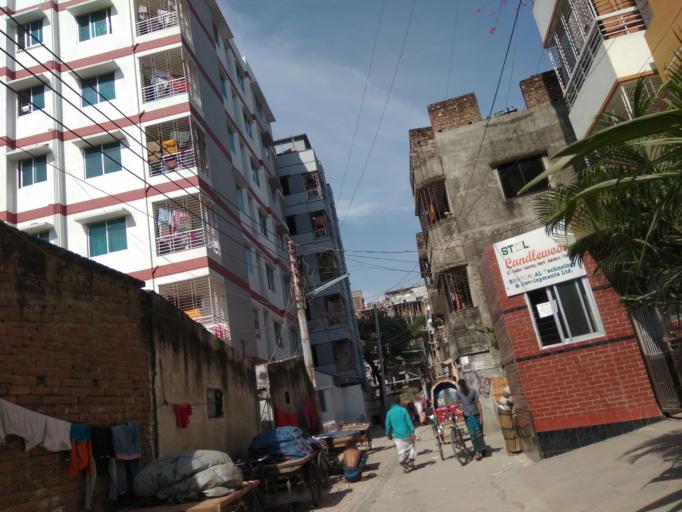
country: BD
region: Dhaka
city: Azimpur
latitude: 23.7762
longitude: 90.3593
